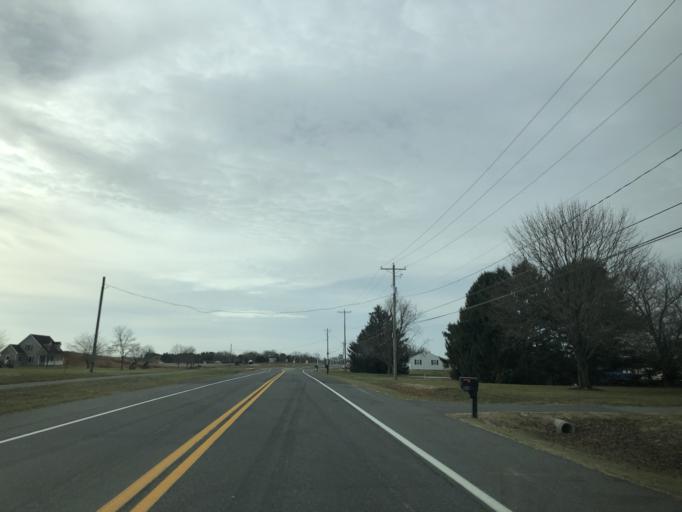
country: US
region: Delaware
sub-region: New Castle County
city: Middletown
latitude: 39.5098
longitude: -75.6805
